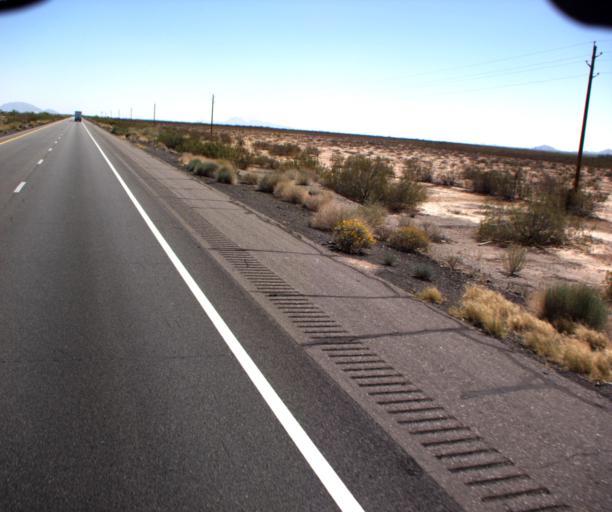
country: US
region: Arizona
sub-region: La Paz County
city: Salome
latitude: 33.5751
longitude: -113.3955
